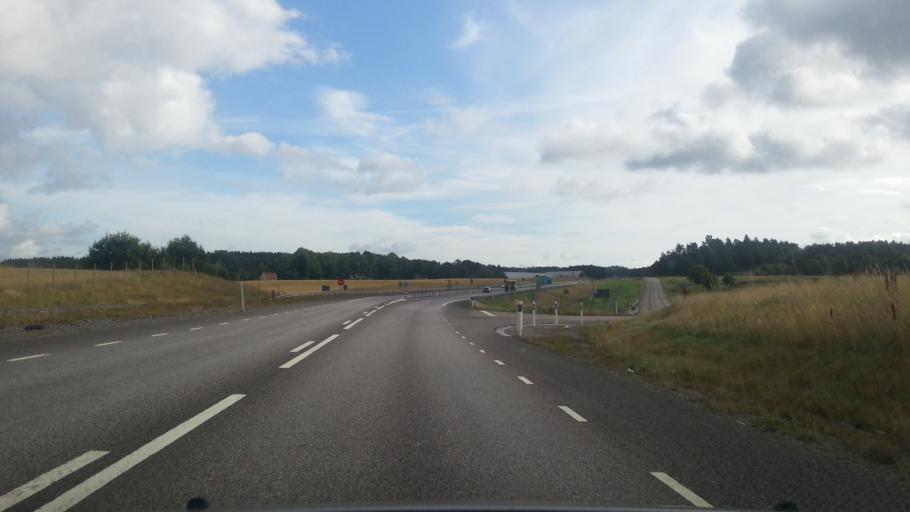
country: SE
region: Vaestra Goetaland
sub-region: Trollhattan
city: Sjuntorp
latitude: 58.2031
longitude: 12.1577
